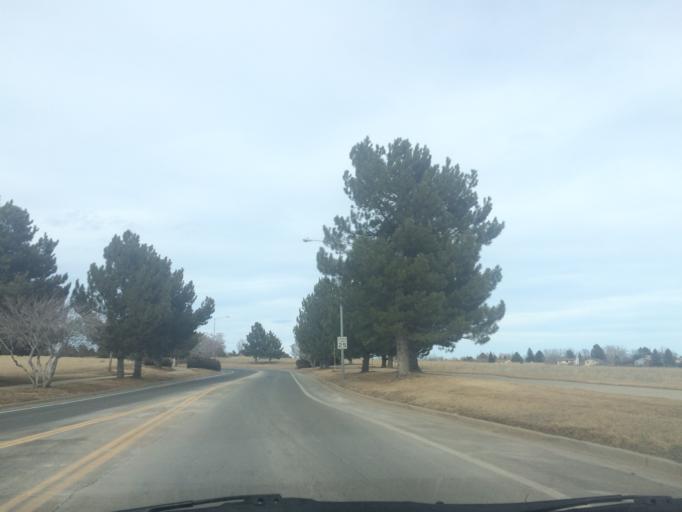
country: US
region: Colorado
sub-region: Broomfield County
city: Broomfield
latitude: 39.9221
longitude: -105.0667
